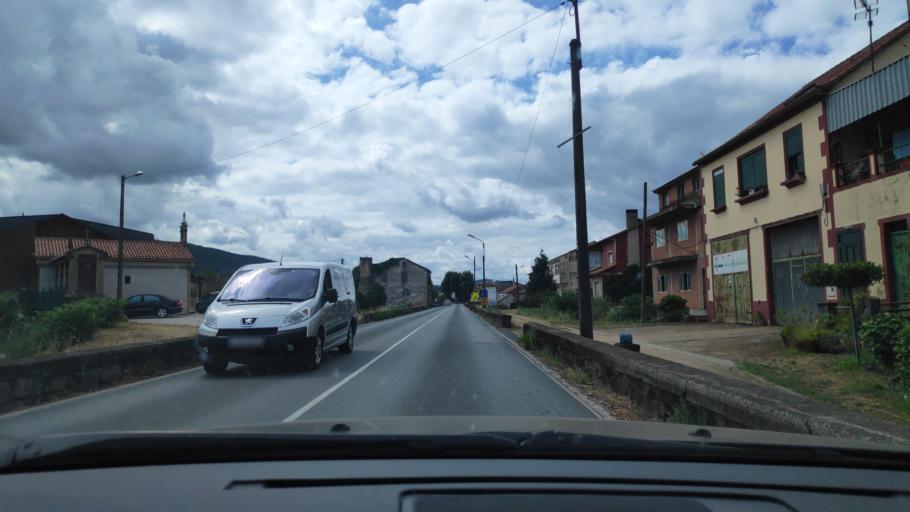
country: ES
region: Galicia
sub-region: Provincia da Coruna
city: Padron
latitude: 42.7276
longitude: -8.6567
